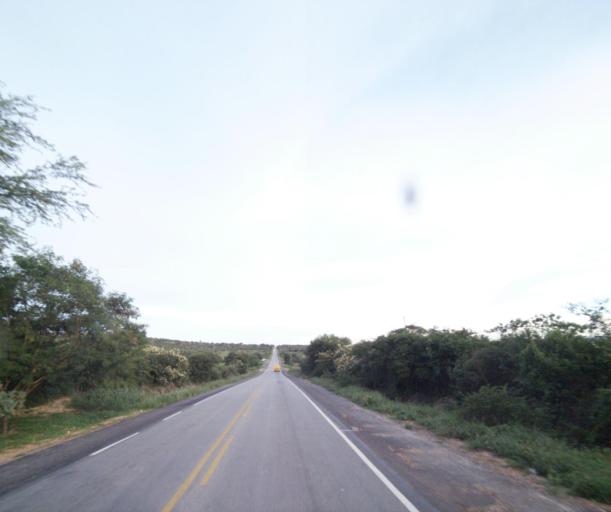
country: BR
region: Bahia
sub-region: Brumado
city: Brumado
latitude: -14.2386
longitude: -41.8851
